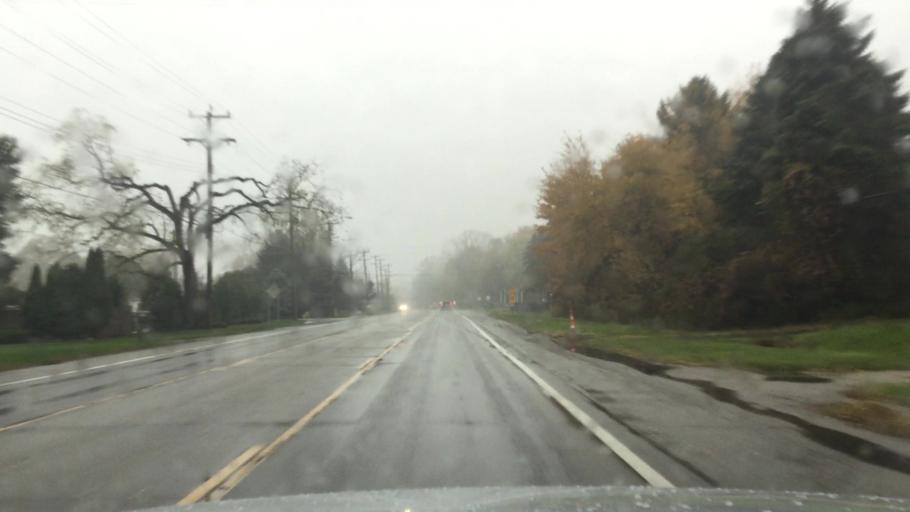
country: US
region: Michigan
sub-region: Macomb County
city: New Baltimore
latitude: 42.6893
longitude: -82.7053
